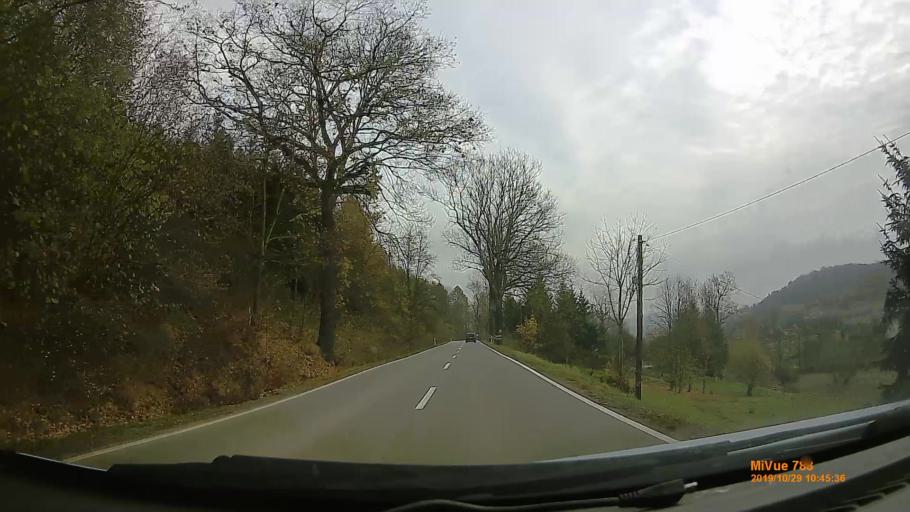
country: PL
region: Lower Silesian Voivodeship
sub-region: Powiat klodzki
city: Radkow
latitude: 50.5523
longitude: 16.4143
